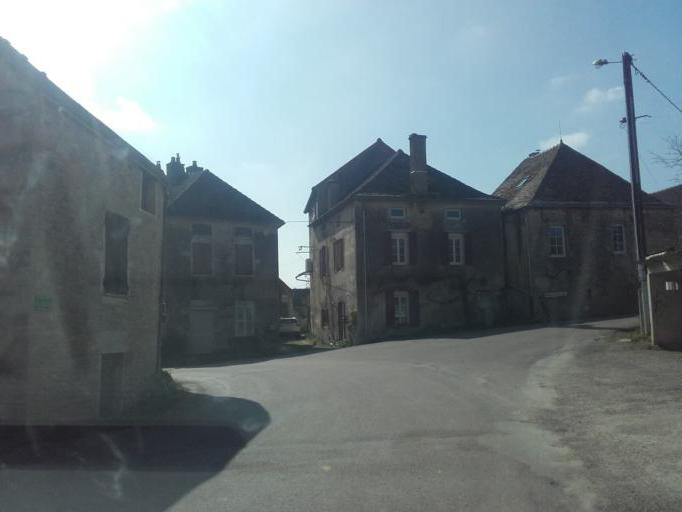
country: FR
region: Bourgogne
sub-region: Departement de la Cote-d'Or
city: Meursault
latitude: 47.0328
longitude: 4.7603
